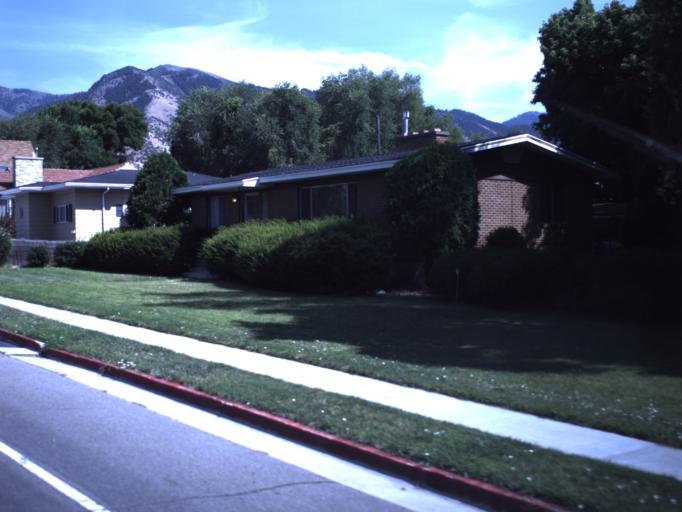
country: US
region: Utah
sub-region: Cache County
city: Logan
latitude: 41.7387
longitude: -111.8183
